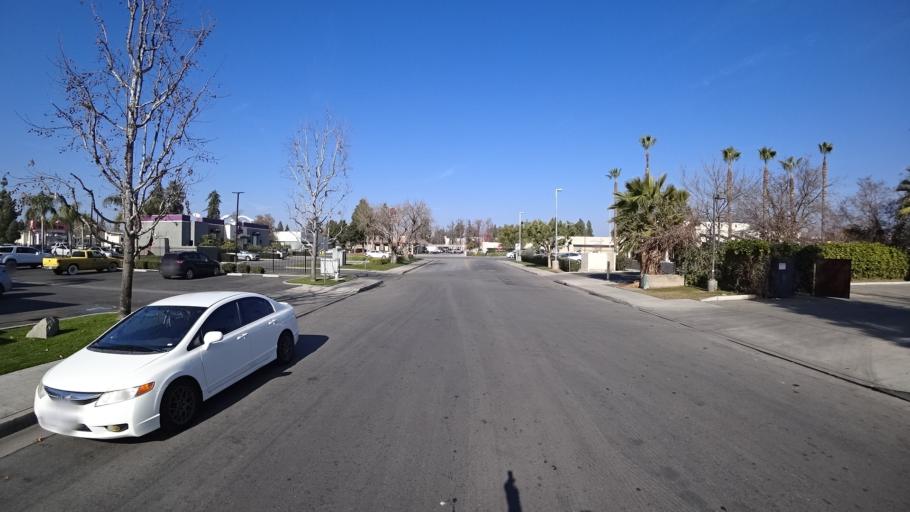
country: US
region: California
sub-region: Kern County
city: Bakersfield
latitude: 35.3388
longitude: -119.0542
